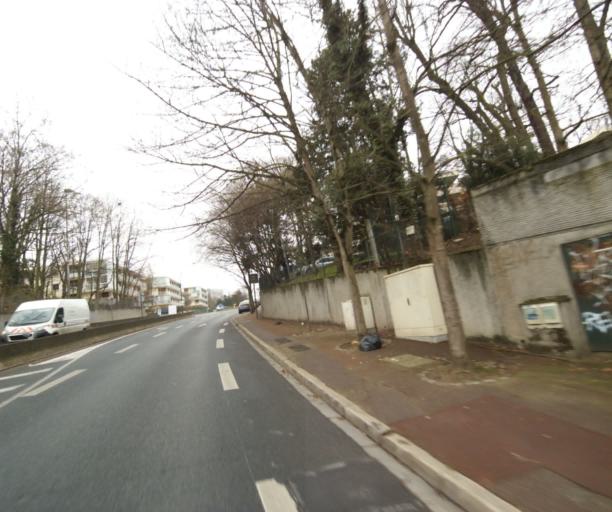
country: FR
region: Ile-de-France
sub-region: Departement des Yvelines
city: Bougival
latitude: 48.8650
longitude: 2.1541
